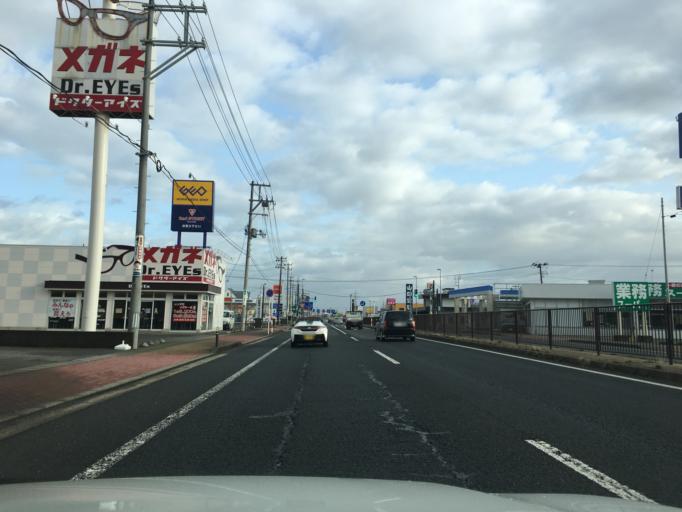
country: JP
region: Yamagata
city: Sakata
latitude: 38.9035
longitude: 139.8564
